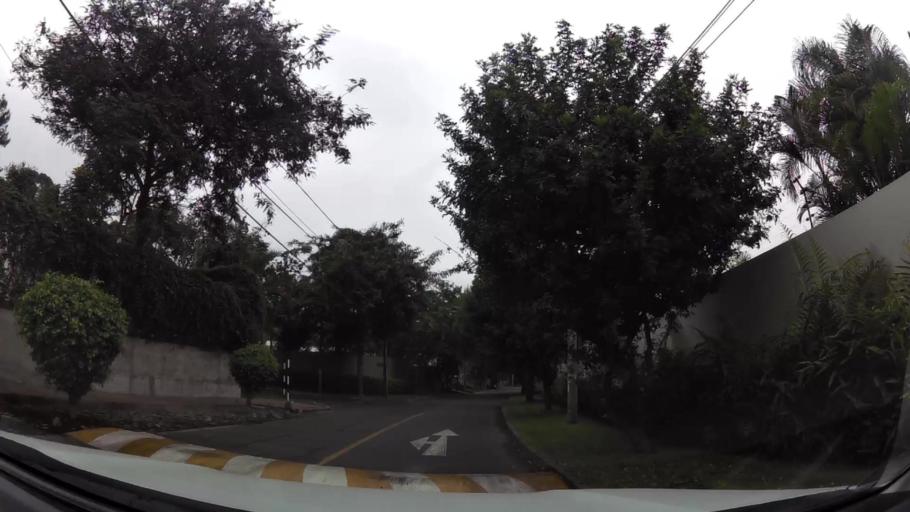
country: PE
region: Lima
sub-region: Lima
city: La Molina
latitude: -12.0713
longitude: -76.9106
